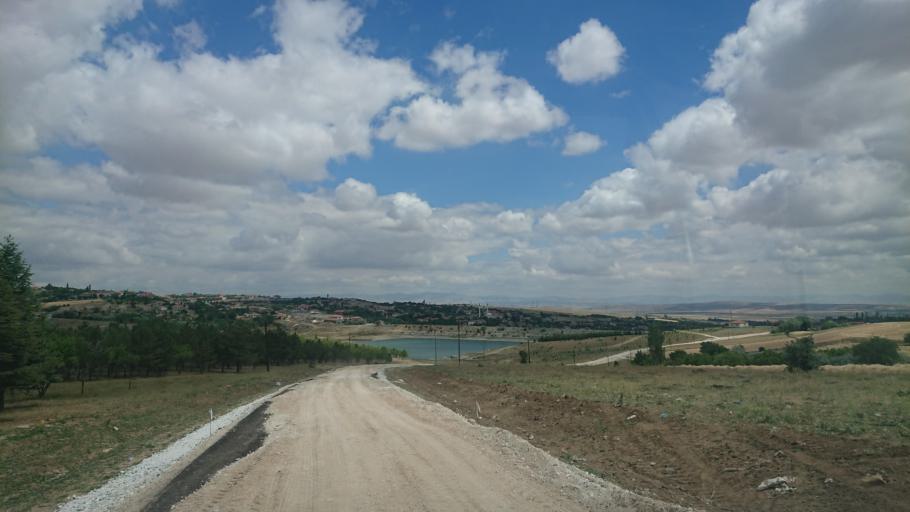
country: TR
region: Aksaray
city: Agacoren
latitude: 38.8595
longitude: 33.9478
